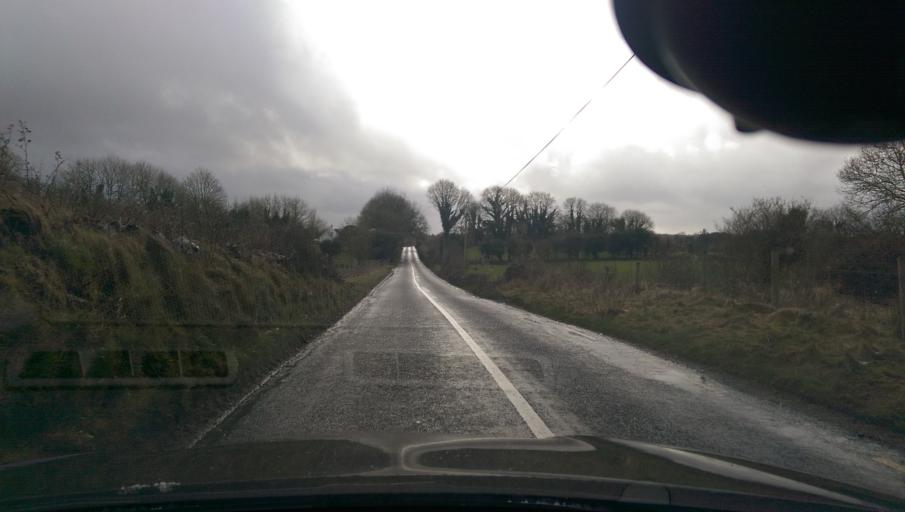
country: IE
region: Connaught
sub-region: County Galway
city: Athenry
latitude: 53.3949
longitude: -8.6576
